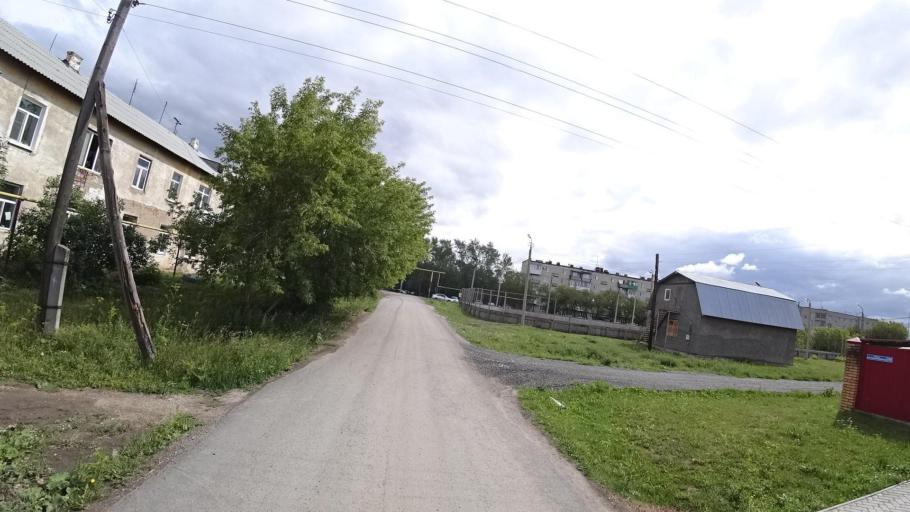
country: RU
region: Sverdlovsk
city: Kamyshlov
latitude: 56.8541
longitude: 62.7130
